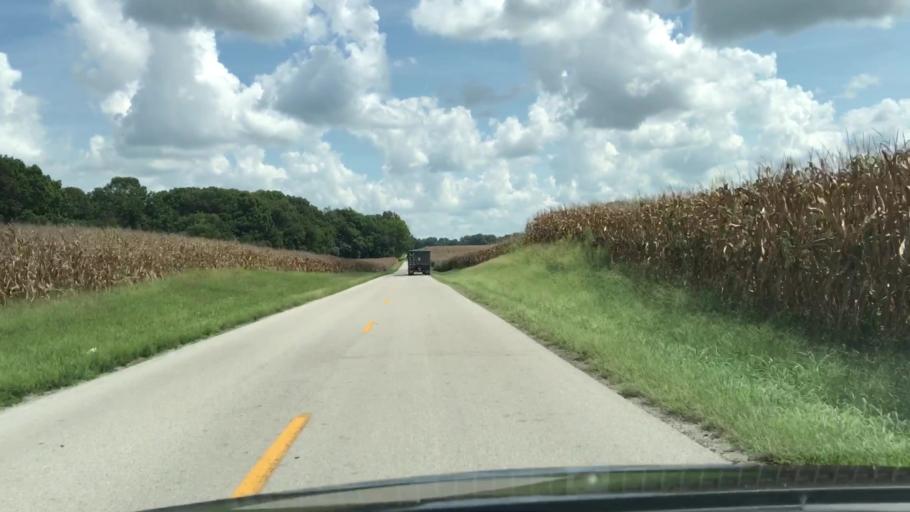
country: US
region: Kentucky
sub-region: Todd County
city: Guthrie
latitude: 36.6491
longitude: -86.9922
